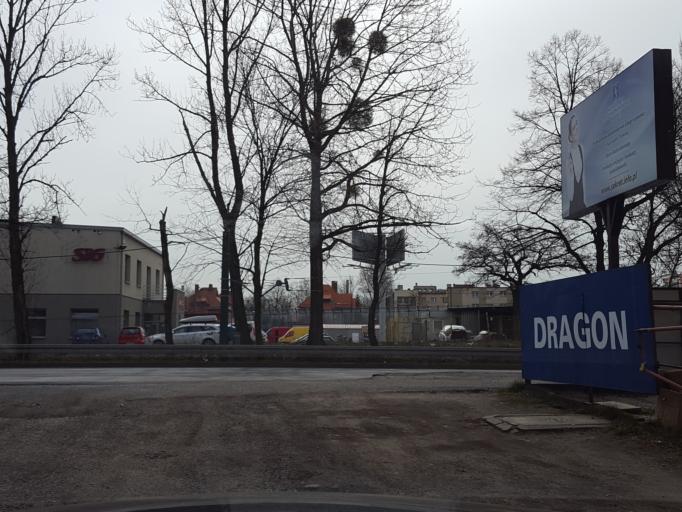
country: PL
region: Silesian Voivodeship
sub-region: Swietochlowice
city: Swietochlowice
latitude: 50.3019
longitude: 18.8767
